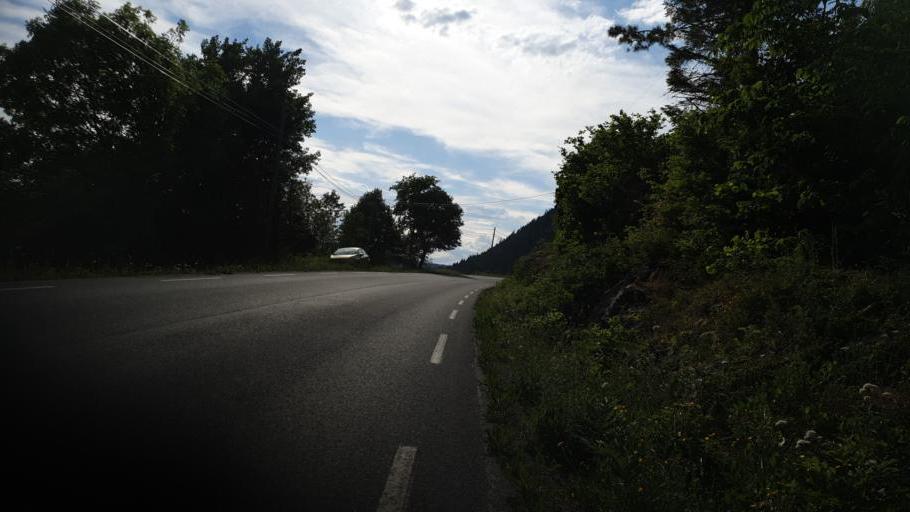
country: NO
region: Sor-Trondelag
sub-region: Trondheim
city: Trondheim
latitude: 63.5568
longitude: 10.2848
